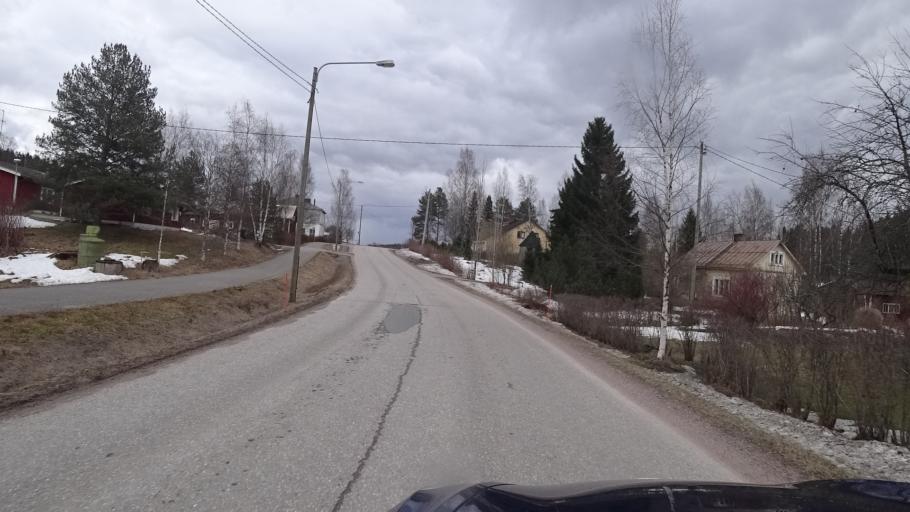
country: FI
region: Paijanne Tavastia
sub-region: Lahti
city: Nastola
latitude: 60.8708
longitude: 26.0103
